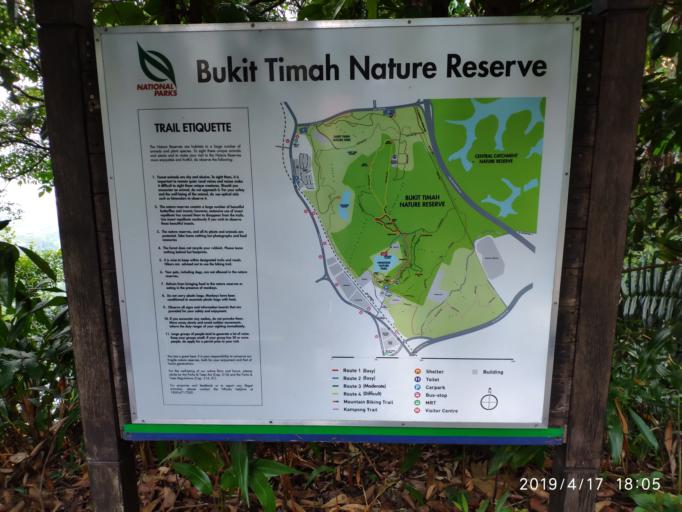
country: SG
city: Singapore
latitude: 1.3519
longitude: 103.7766
